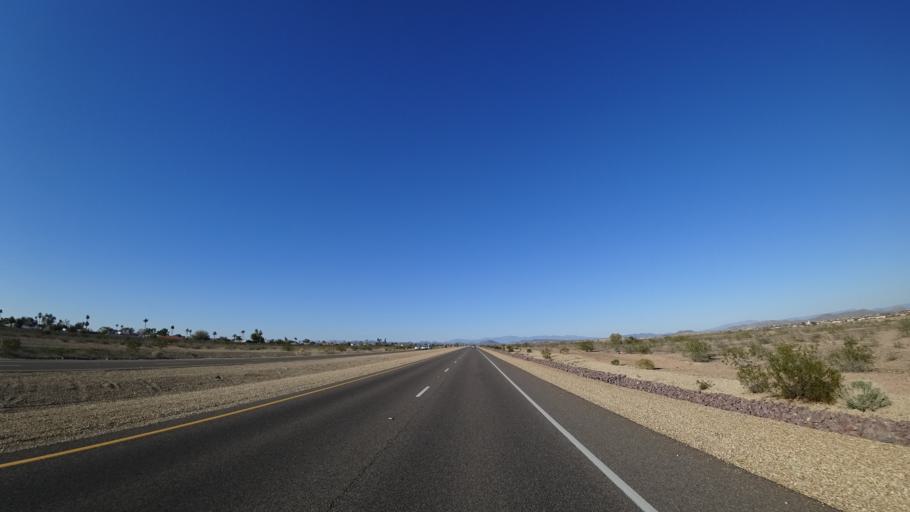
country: US
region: Arizona
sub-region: Maricopa County
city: Sun City West
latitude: 33.6517
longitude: -112.3228
